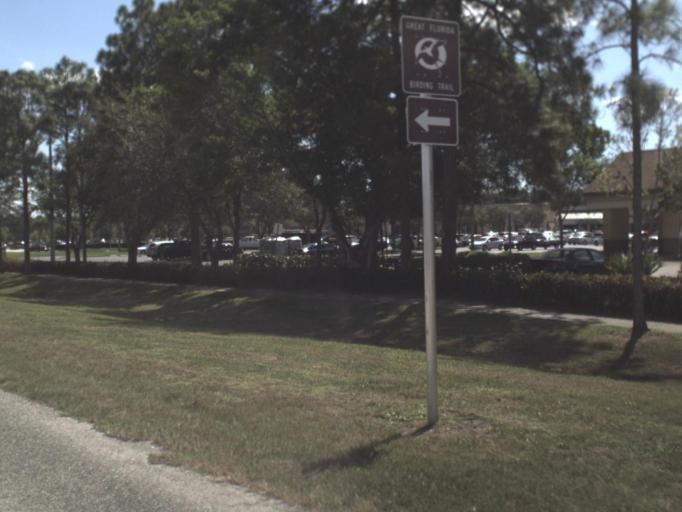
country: US
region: Florida
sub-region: Collier County
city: Lely Resort
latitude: 26.0655
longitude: -81.7029
